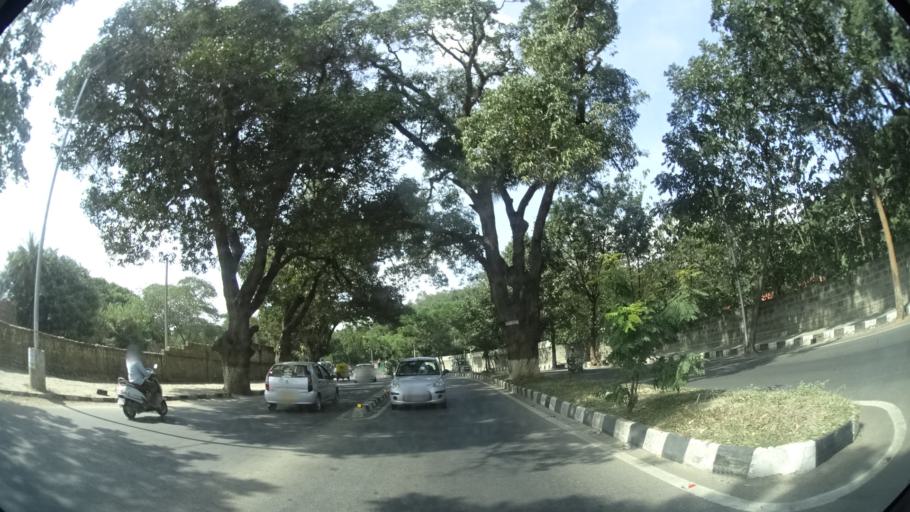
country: IN
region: Karnataka
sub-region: Bangalore Urban
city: Bangalore
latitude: 13.0137
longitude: 77.5879
